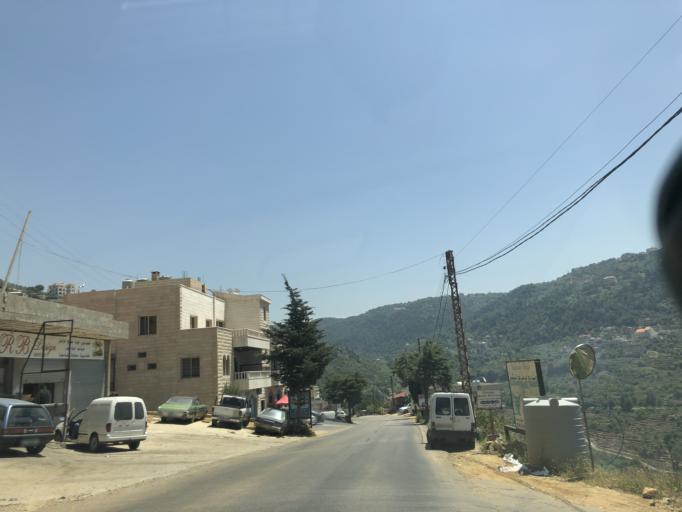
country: LB
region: Mont-Liban
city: Beit ed Dine
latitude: 33.6907
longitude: 35.5341
